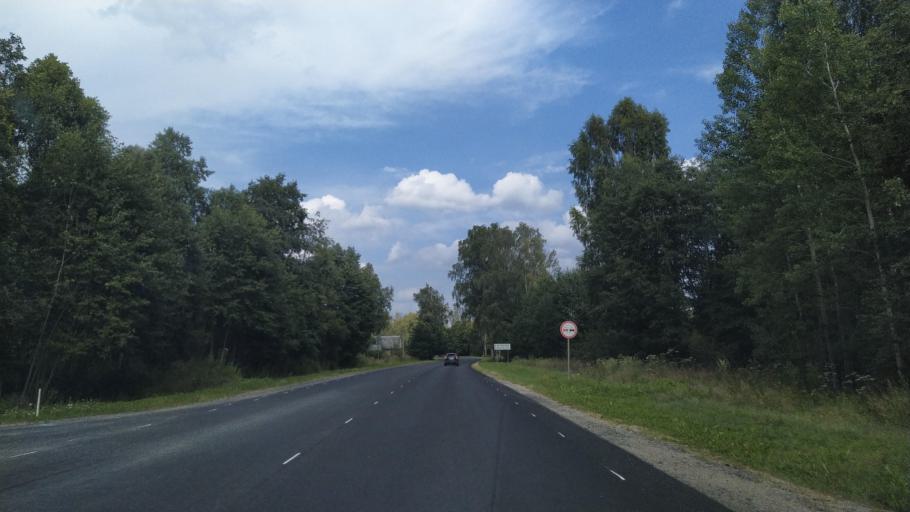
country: RU
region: Pskov
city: Porkhov
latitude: 57.8297
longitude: 29.5292
